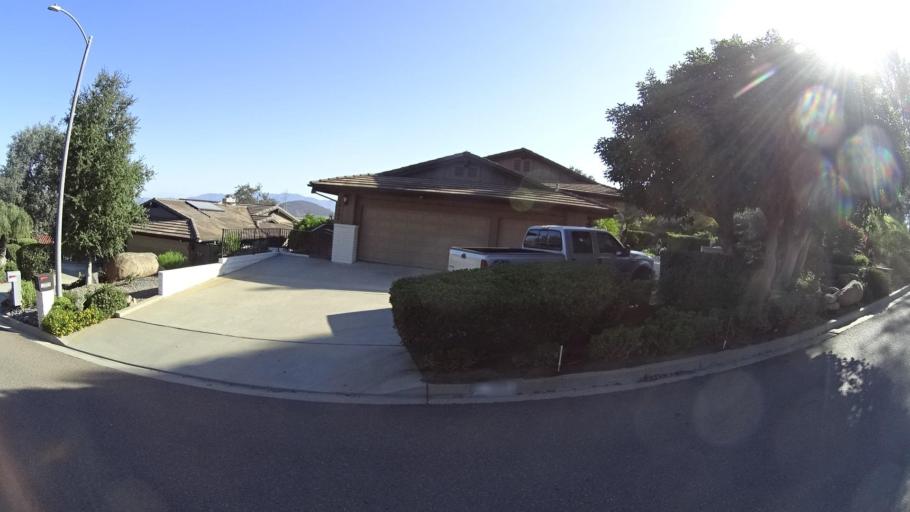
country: US
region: California
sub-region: San Diego County
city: Hidden Meadows
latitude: 33.2187
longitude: -117.0968
